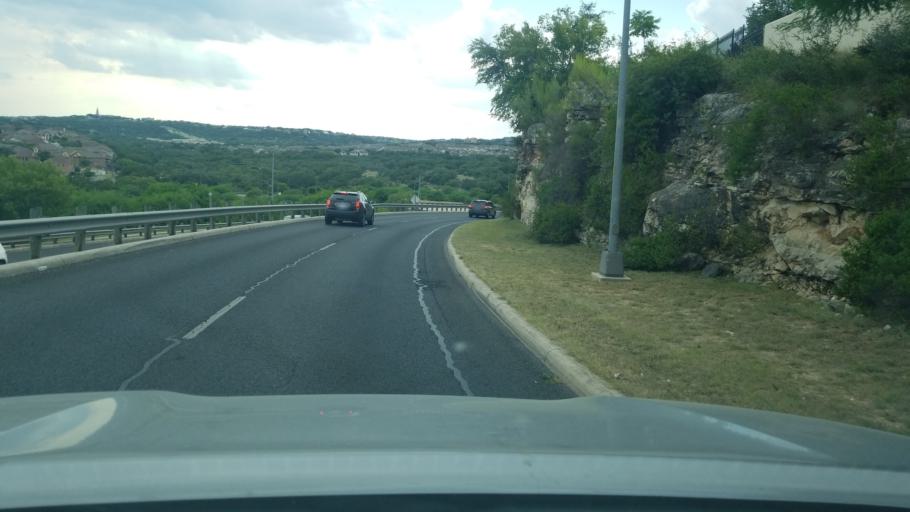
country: US
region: Texas
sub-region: Bexar County
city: Hollywood Park
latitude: 29.6392
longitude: -98.4643
